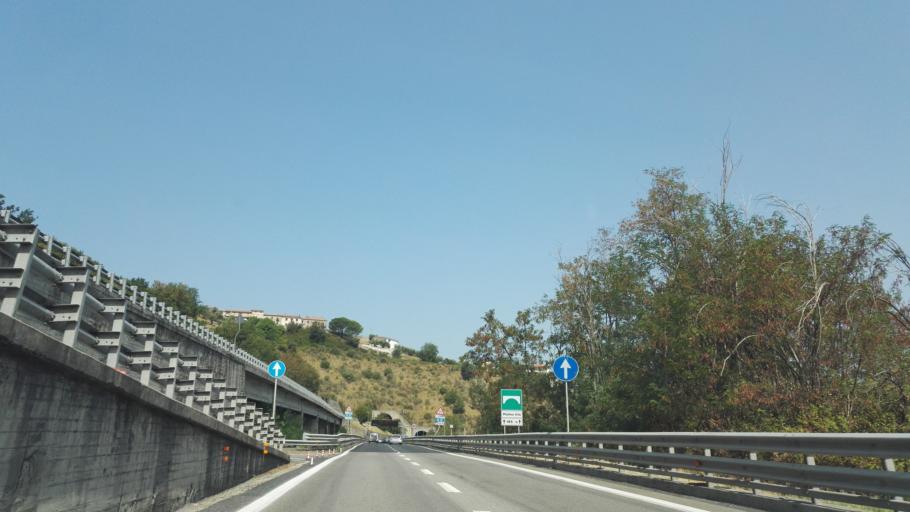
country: IT
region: Calabria
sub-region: Provincia di Cosenza
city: Laurignano
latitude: 39.2810
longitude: 16.2472
